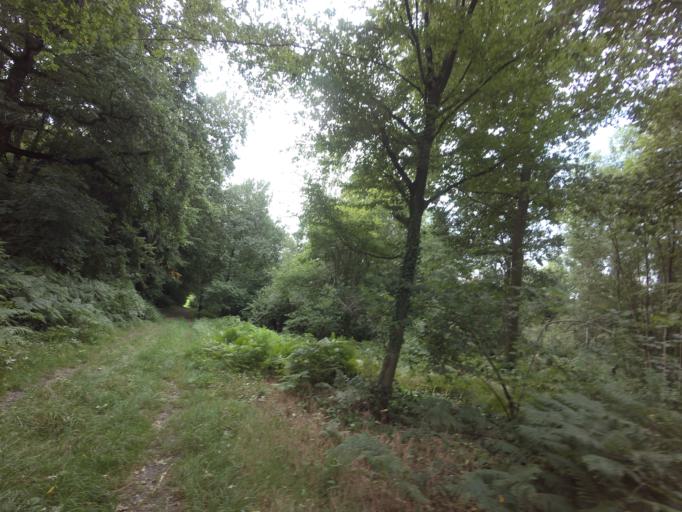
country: NL
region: Limburg
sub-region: Gemeente Simpelveld
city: Simpelveld
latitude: 50.7975
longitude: 5.9898
